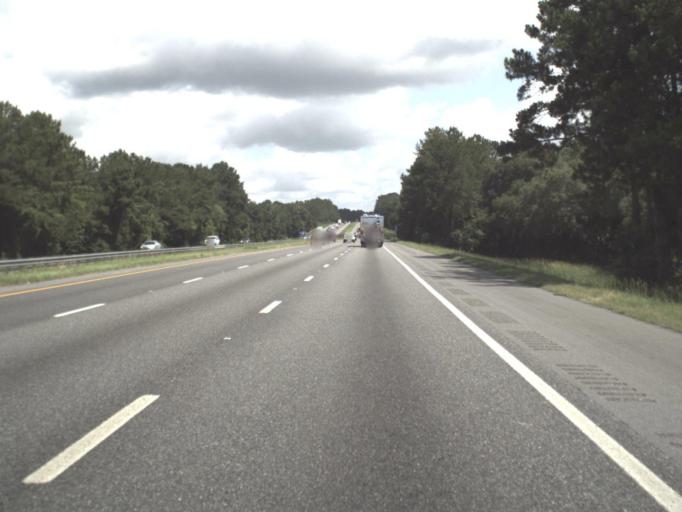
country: US
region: Florida
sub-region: Alachua County
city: High Springs
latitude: 29.9292
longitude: -82.5597
